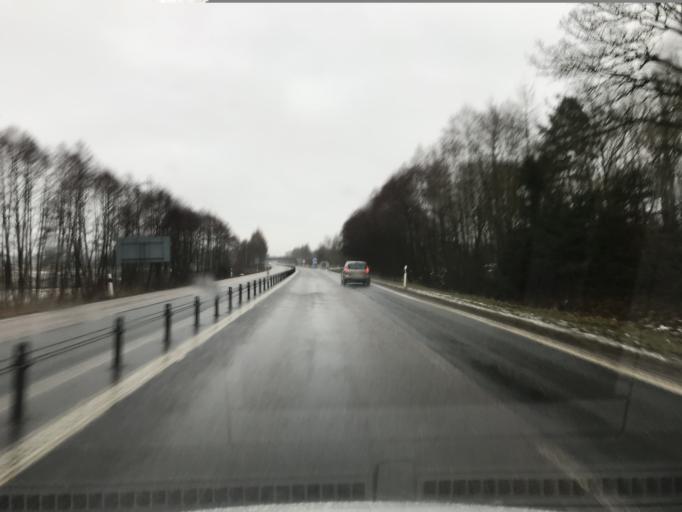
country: SE
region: Skane
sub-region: Hassleholms Kommun
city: Tormestorp
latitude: 56.1740
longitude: 13.6791
